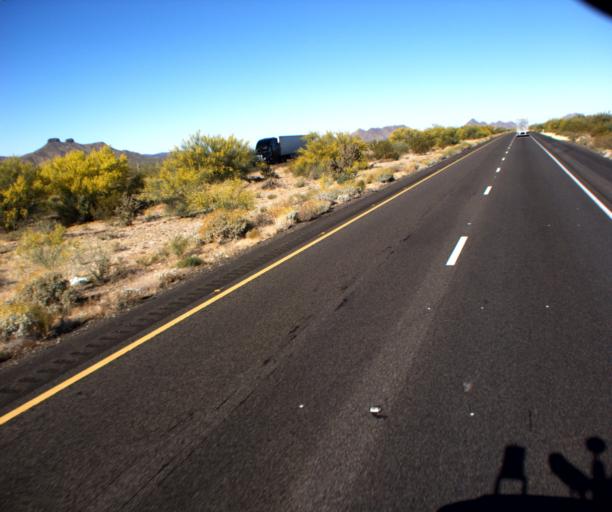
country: US
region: Arizona
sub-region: Maricopa County
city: Gila Bend
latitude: 32.8684
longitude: -112.4253
